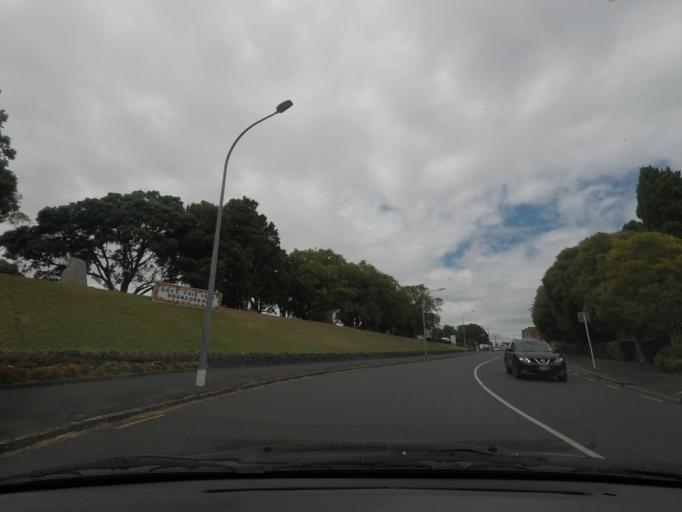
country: NZ
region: Auckland
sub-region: Auckland
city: Auckland
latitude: -36.8490
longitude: 174.7858
